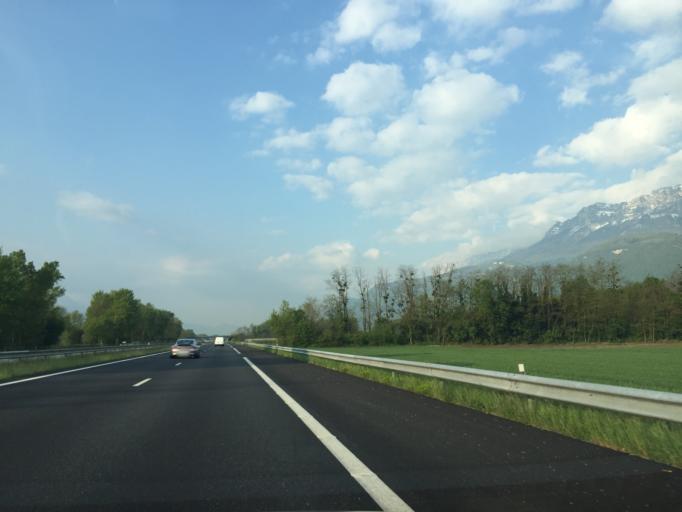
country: FR
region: Rhone-Alpes
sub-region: Departement de l'Isere
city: Le Cheylas
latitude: 45.4010
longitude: 5.9939
